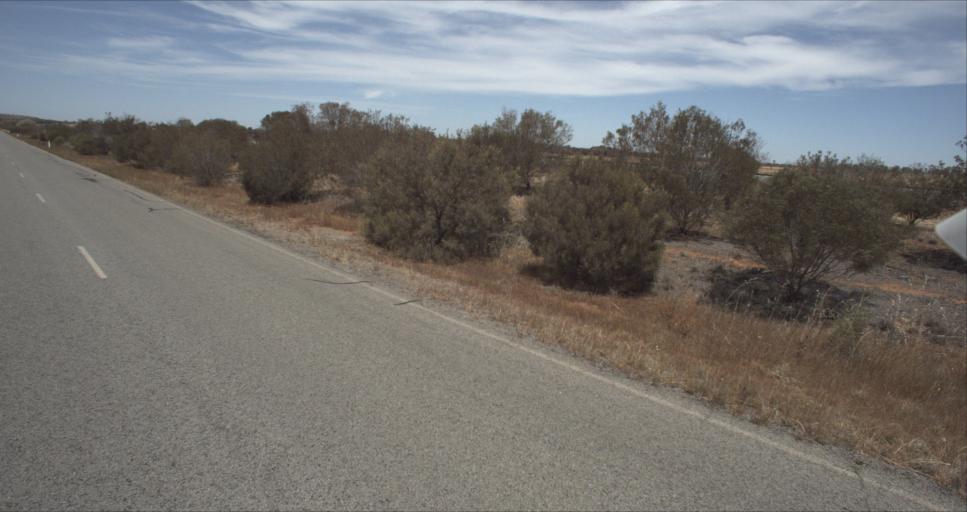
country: AU
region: New South Wales
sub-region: Leeton
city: Leeton
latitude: -34.6246
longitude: 146.4500
